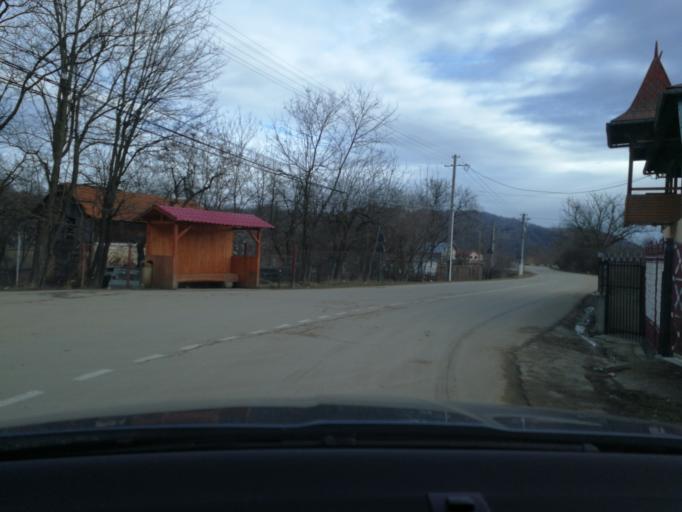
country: RO
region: Prahova
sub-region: Comuna Adunati
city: Ocina de Sus
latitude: 45.1832
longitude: 25.5982
